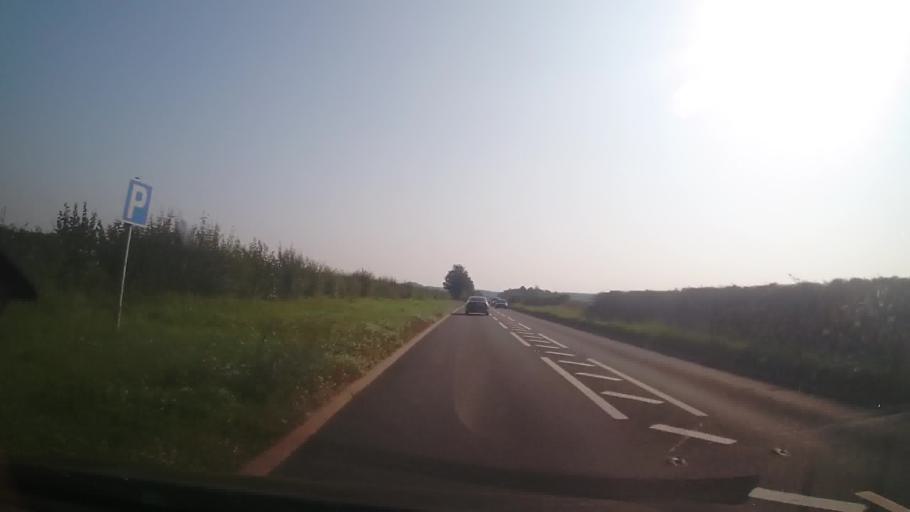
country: GB
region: England
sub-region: Shropshire
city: Bridgnorth
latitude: 52.5416
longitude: -2.4791
